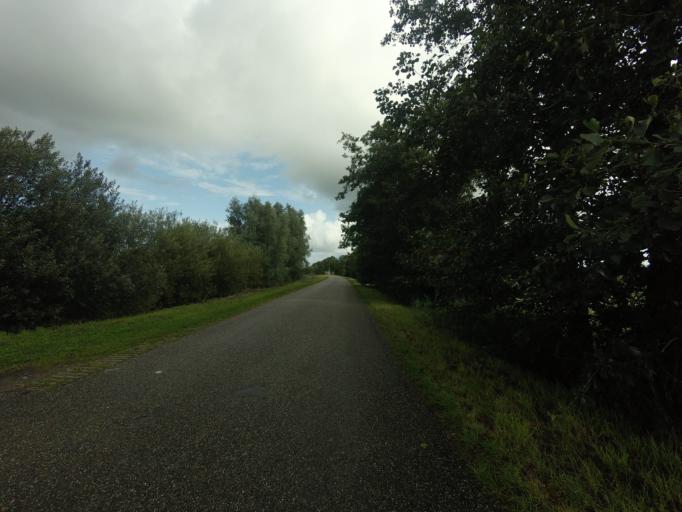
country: NL
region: Friesland
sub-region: Gemeente Tytsjerksteradiel
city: Garyp
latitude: 53.1530
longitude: 5.9500
